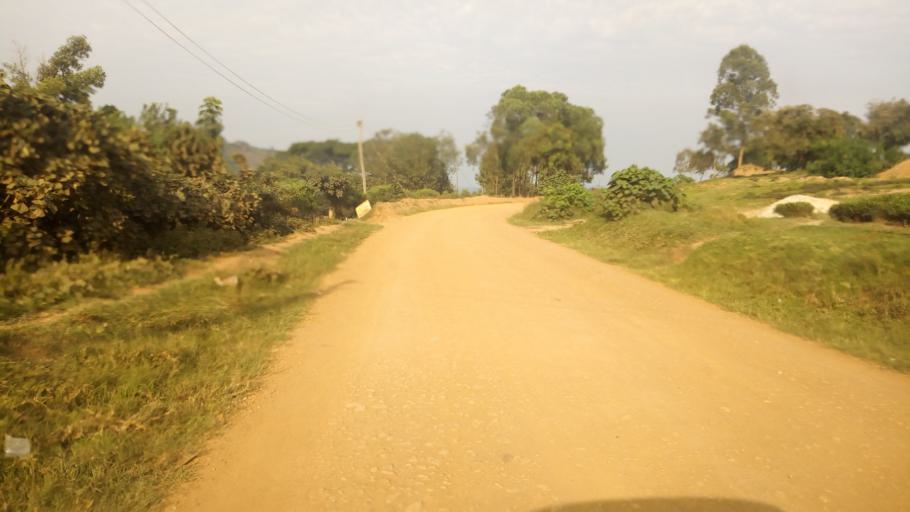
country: UG
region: Western Region
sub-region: Kanungu District
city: Ntungamo
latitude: -0.8363
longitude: 29.6825
